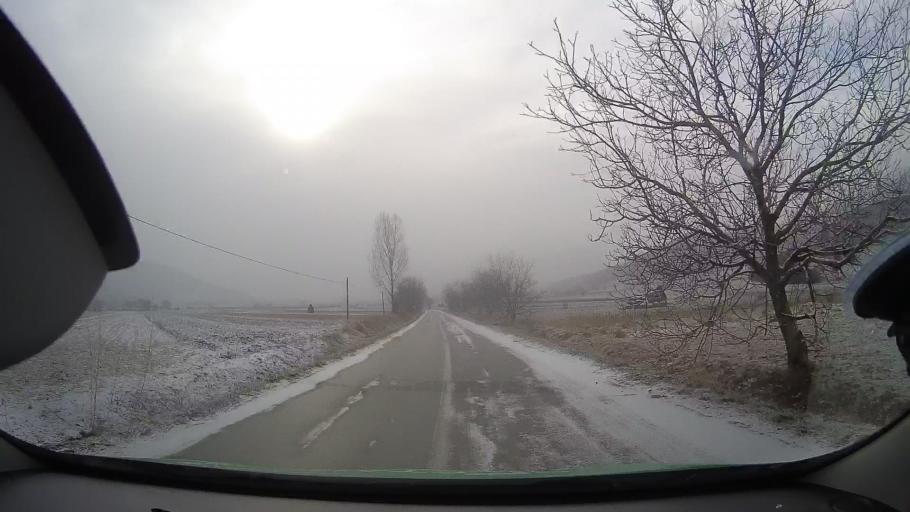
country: RO
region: Alba
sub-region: Comuna Rimetea
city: Rimetea
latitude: 46.4165
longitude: 23.5581
